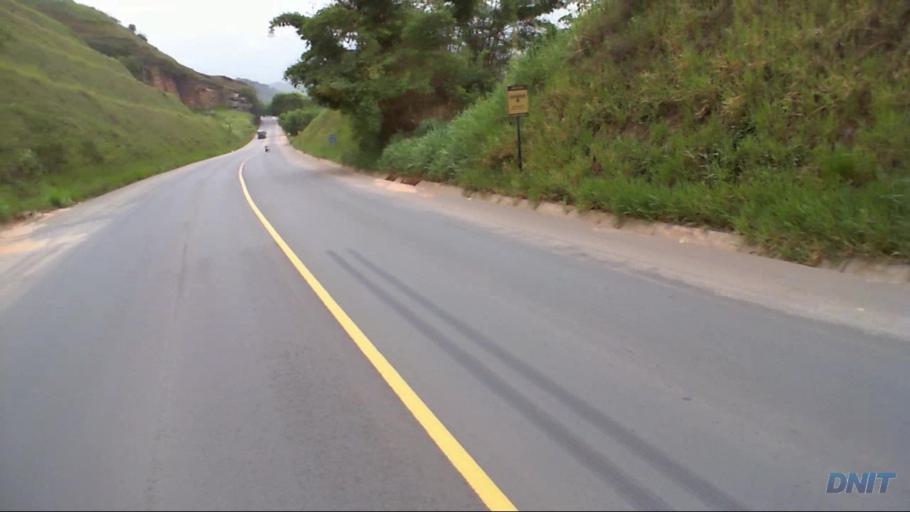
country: BR
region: Minas Gerais
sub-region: Coronel Fabriciano
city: Coronel Fabriciano
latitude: -19.5264
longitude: -42.6678
